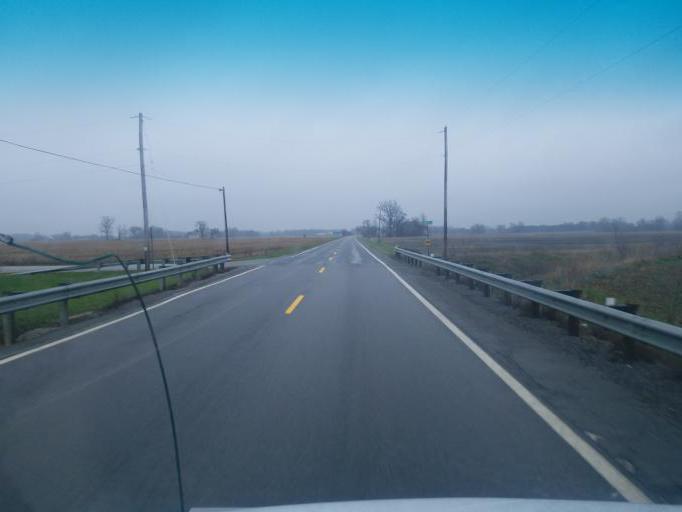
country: US
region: Ohio
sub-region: Wood County
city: Bowling Green
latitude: 41.3721
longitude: -83.7238
